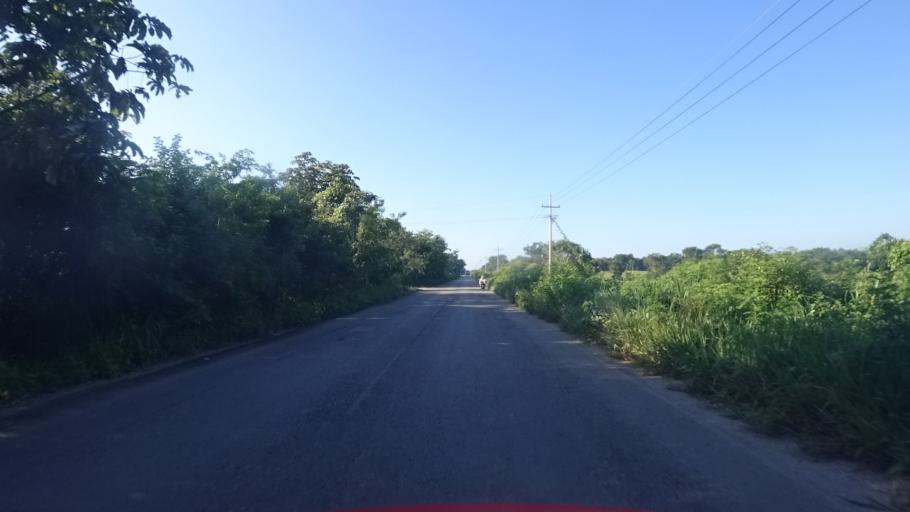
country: MX
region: Yucatan
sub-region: Tizimin
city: Tizimin
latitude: 21.1423
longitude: -88.1834
